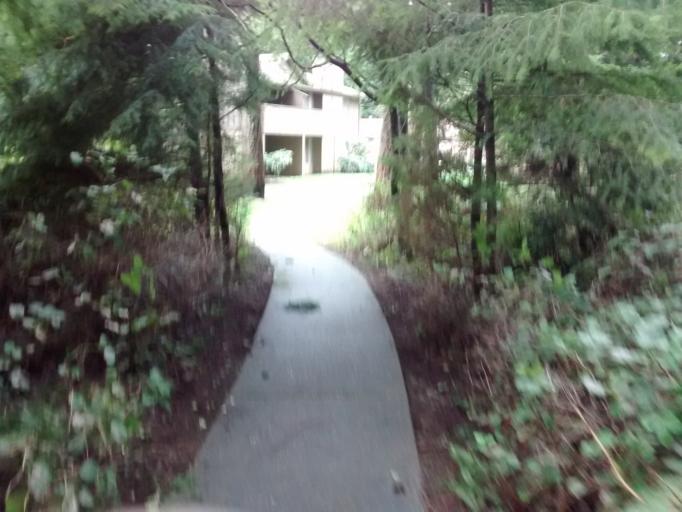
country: US
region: Washington
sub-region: Kitsap County
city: Parkwood
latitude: 47.5215
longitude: -122.6088
